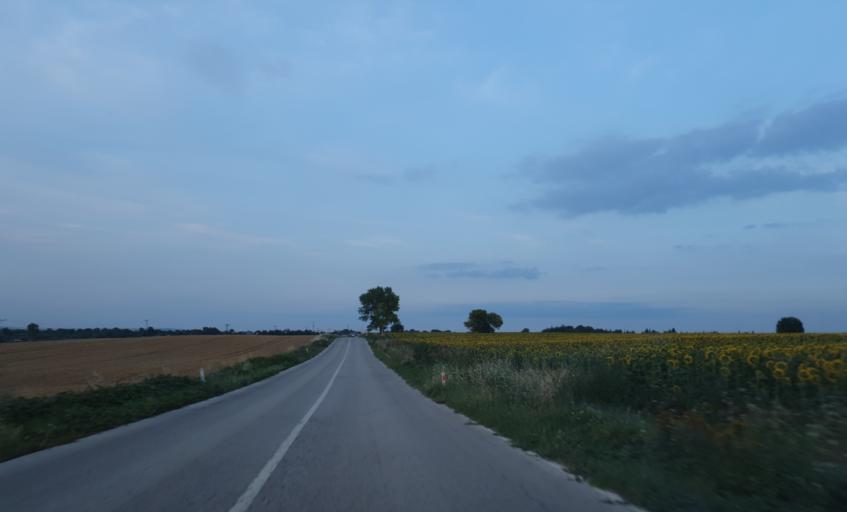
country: TR
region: Tekirdag
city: Beyazkoy
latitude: 41.4033
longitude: 27.6422
